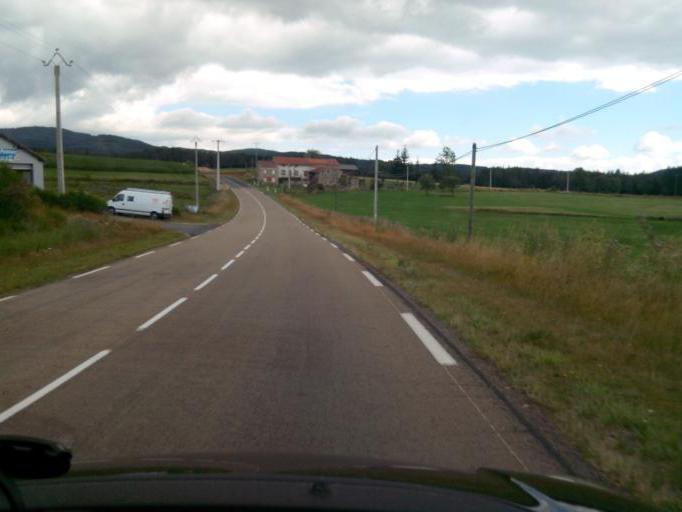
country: FR
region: Rhone-Alpes
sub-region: Departement de la Loire
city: Usson-en-Forez
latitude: 45.3972
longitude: 3.9487
